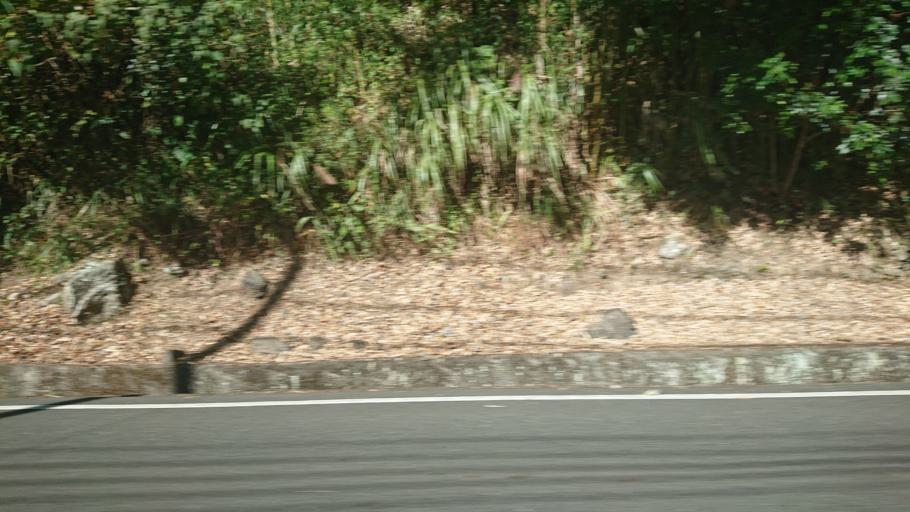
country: TW
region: Taiwan
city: Lugu
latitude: 23.4886
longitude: 120.7531
